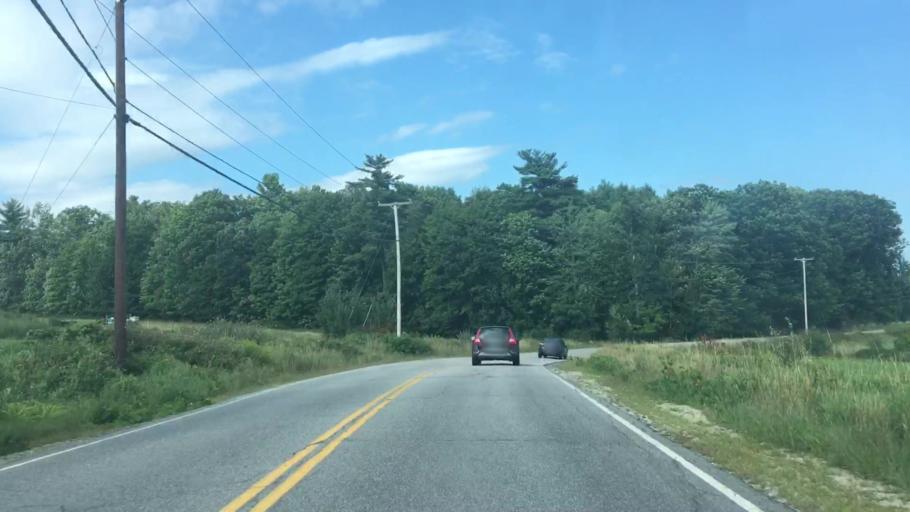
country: US
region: Maine
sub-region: Oxford County
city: Oxford
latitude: 44.1301
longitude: -70.5029
